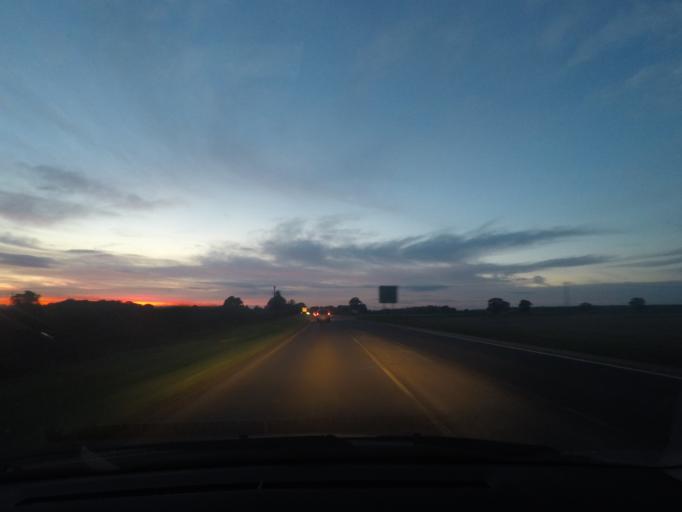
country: GB
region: England
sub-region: City of York
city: Elvington
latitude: 53.9508
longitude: -0.9443
